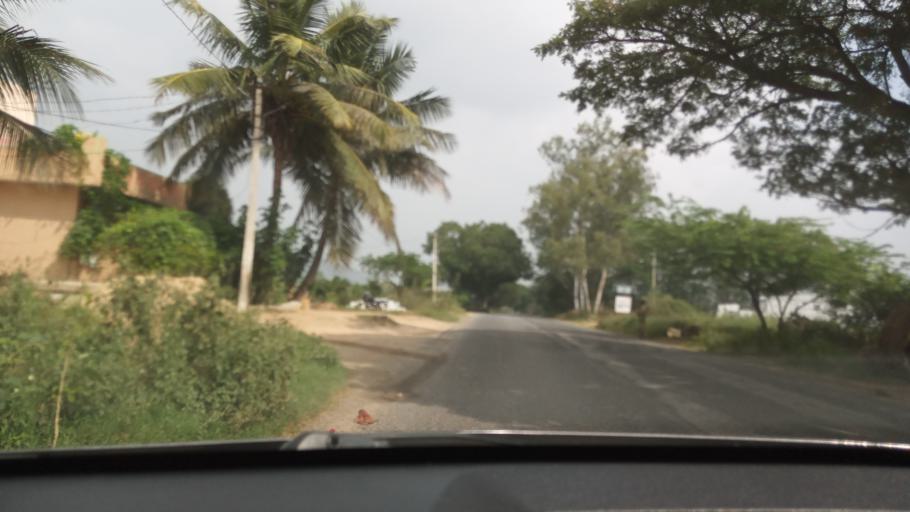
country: IN
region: Andhra Pradesh
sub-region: Chittoor
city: Madanapalle
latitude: 13.6517
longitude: 78.8184
